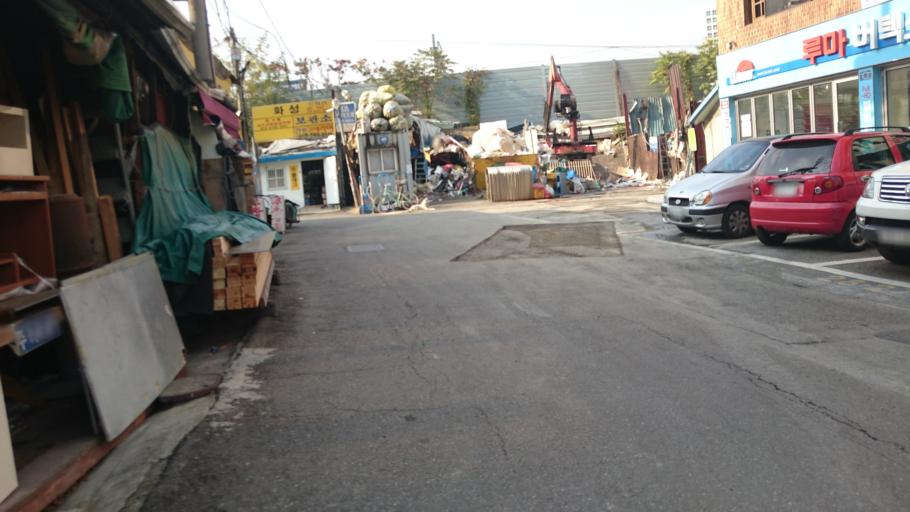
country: KR
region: Seoul
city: Seoul
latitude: 37.5310
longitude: 126.9681
